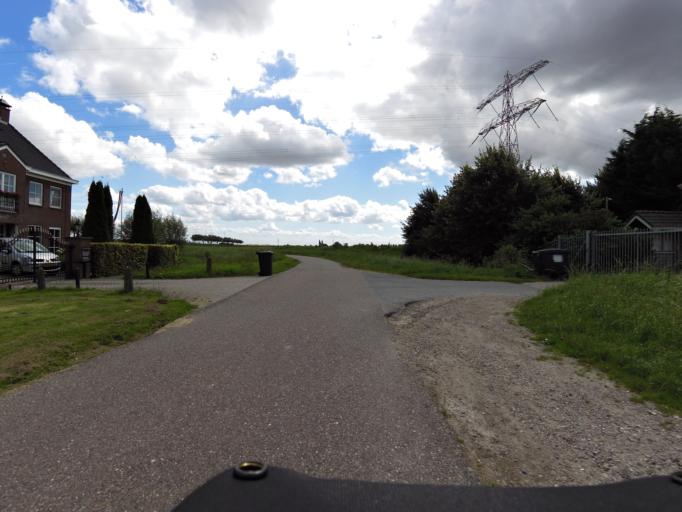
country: NL
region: South Holland
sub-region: Gemeente Spijkenisse
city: Spijkenisse
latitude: 51.8306
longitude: 4.3602
